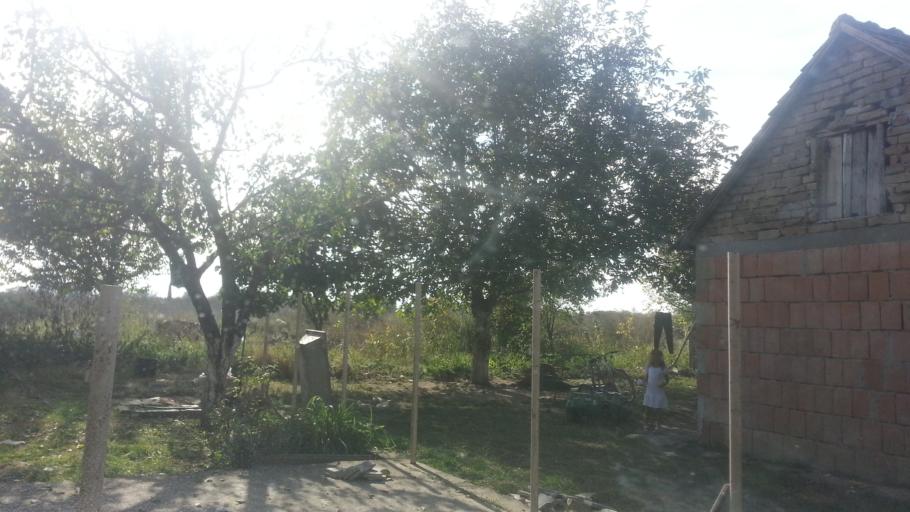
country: RS
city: Belegis
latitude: 45.0238
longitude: 20.3189
